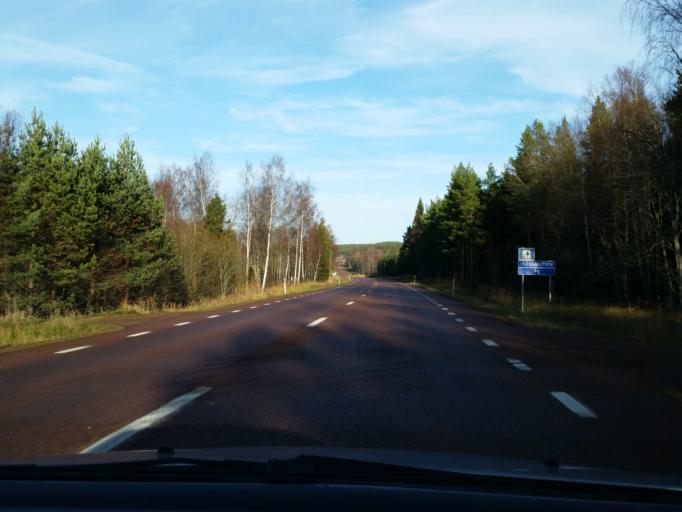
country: AX
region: Alands landsbygd
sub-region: Finstroem
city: Finstroem
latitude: 60.2920
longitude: 19.9534
